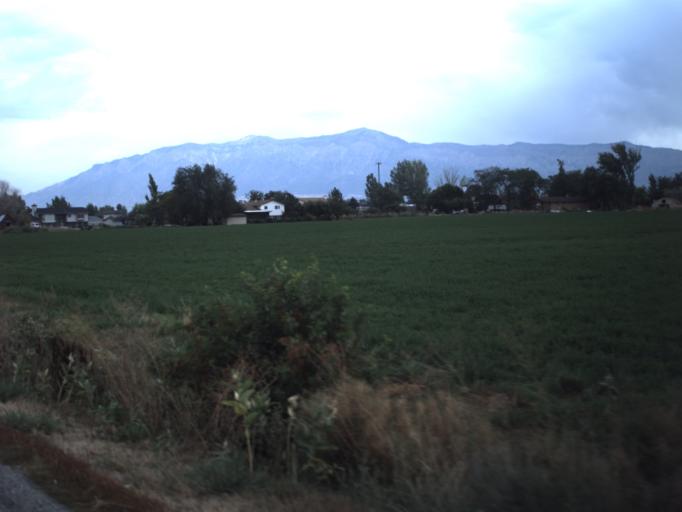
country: US
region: Utah
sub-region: Weber County
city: West Haven
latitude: 41.2399
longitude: -112.0926
